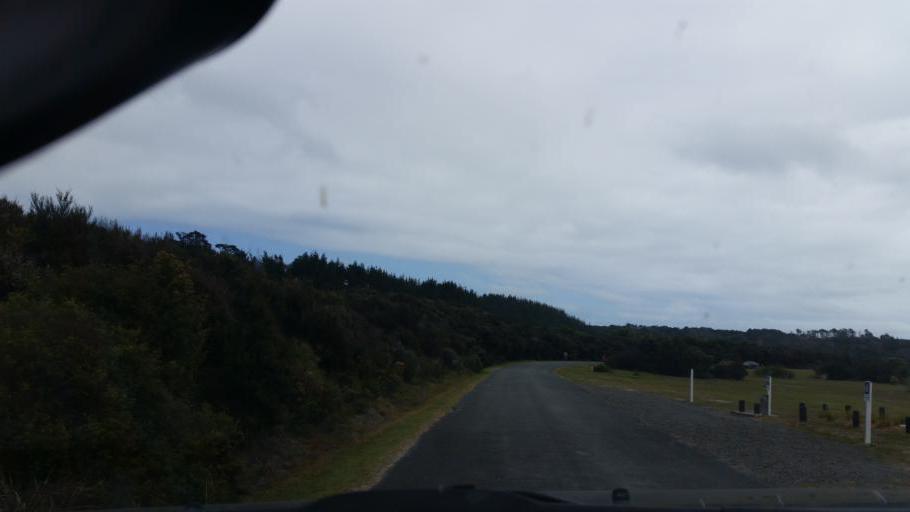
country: NZ
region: Northland
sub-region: Kaipara District
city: Dargaville
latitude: -35.8112
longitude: 173.6617
